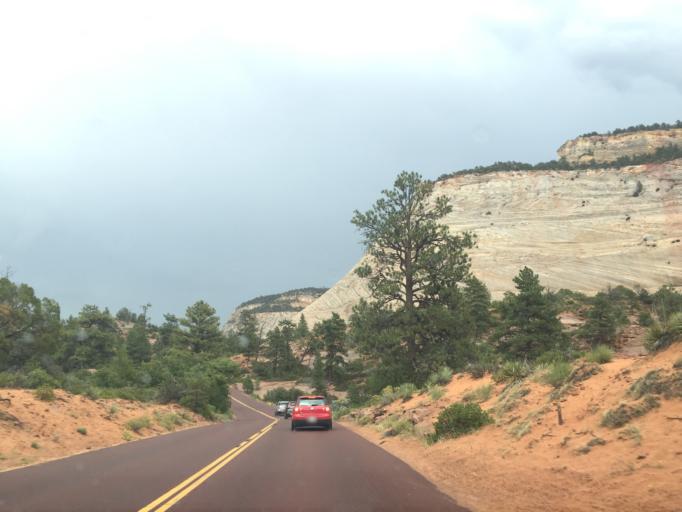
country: US
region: Utah
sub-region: Washington County
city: Hildale
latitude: 37.2259
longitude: -112.8873
